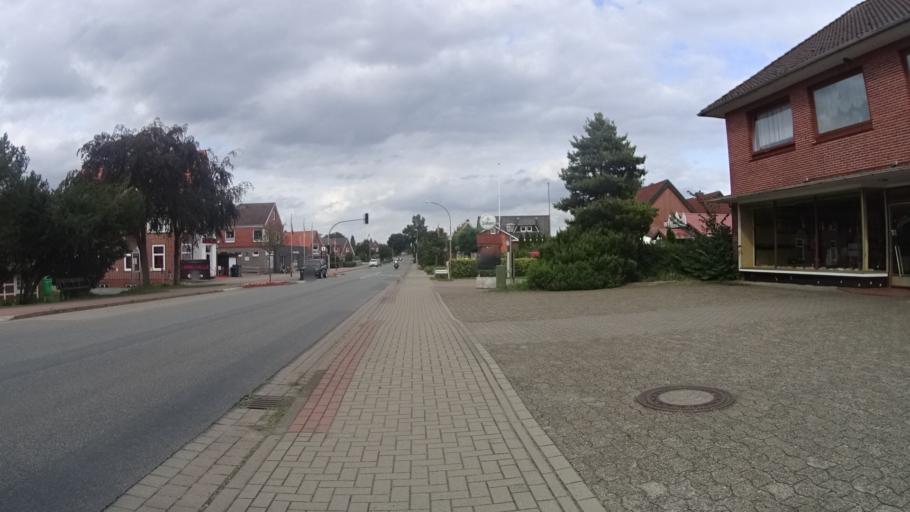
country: DE
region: Lower Saxony
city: Wischhafen
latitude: 53.7749
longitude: 9.3198
